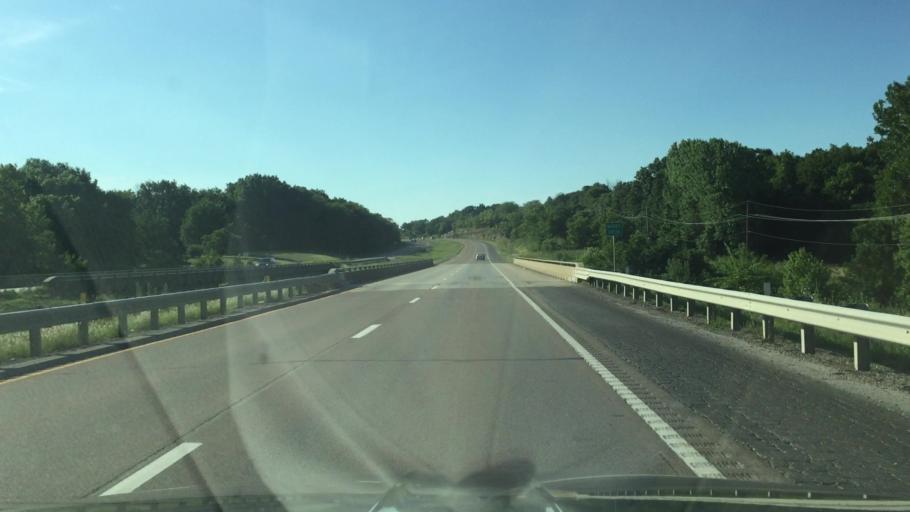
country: US
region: Missouri
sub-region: Pettis County
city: Sedalia
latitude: 38.7281
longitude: -93.3046
